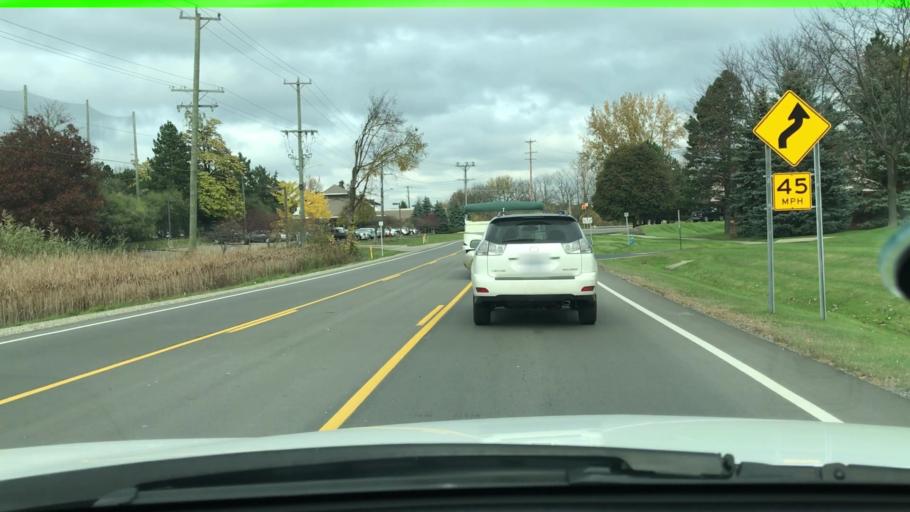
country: US
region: Michigan
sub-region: Oakland County
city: Waterford
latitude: 42.6561
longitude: -83.4438
